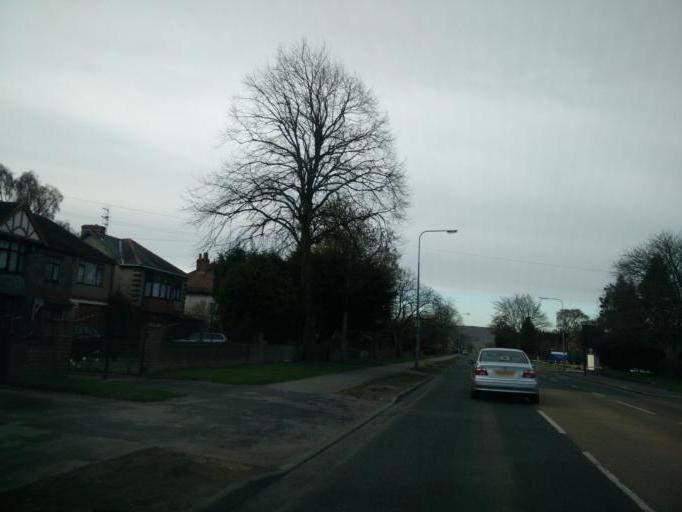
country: GB
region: England
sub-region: County Durham
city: Bishop Auckland
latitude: 54.6496
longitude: -1.6791
